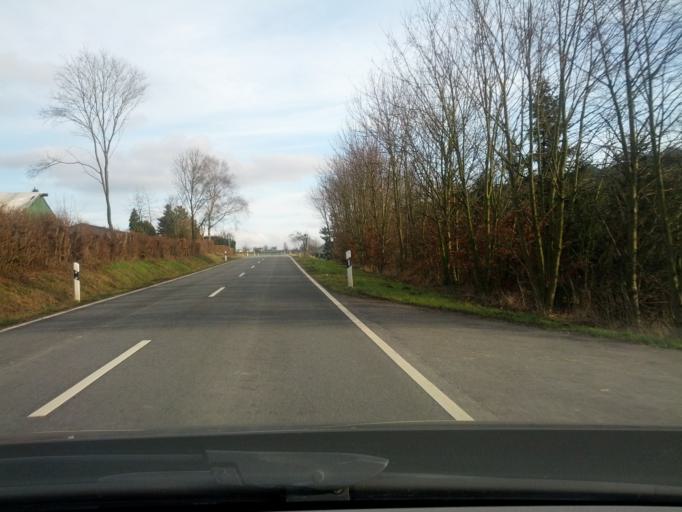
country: DE
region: Hesse
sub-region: Regierungsbezirk Kassel
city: Weissenborn
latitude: 51.0902
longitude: 10.1087
